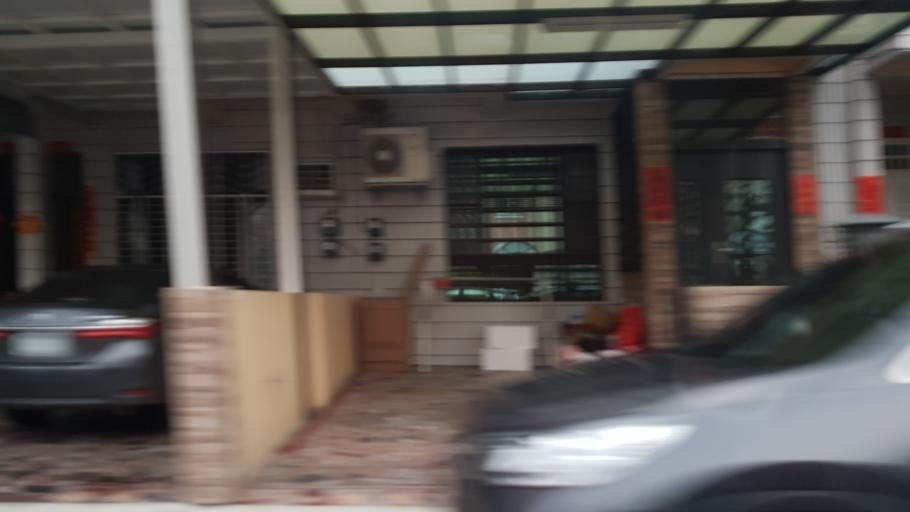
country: TW
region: Taiwan
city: Xinying
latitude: 23.3182
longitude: 120.3147
